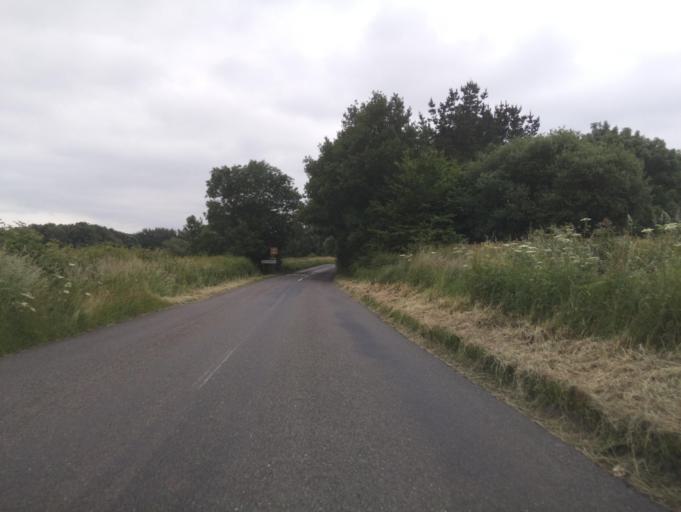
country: GB
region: England
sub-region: Leicestershire
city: Melton Mowbray
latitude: 52.7161
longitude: -0.8296
